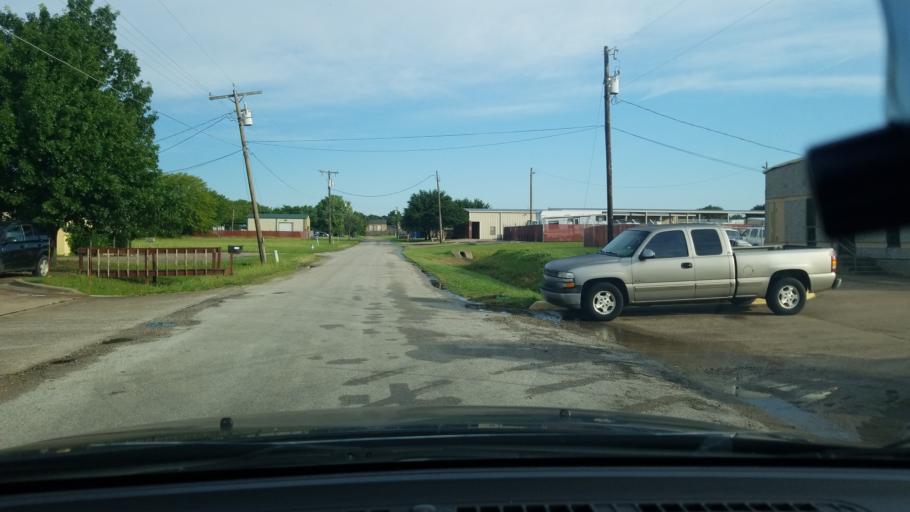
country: US
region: Texas
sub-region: Dallas County
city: Mesquite
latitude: 32.7961
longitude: -96.6190
